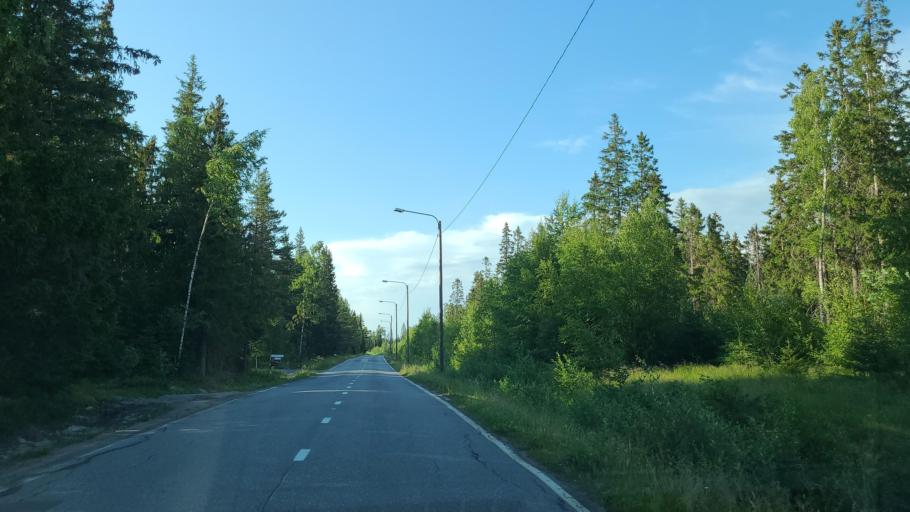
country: FI
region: Ostrobothnia
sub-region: Vaasa
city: Replot
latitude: 63.3565
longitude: 21.3036
